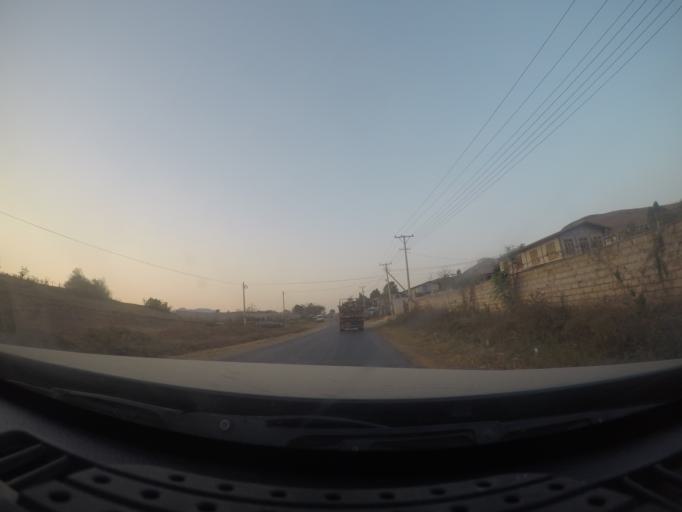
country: MM
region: Shan
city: Taunggyi
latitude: 20.6994
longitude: 97.0597
